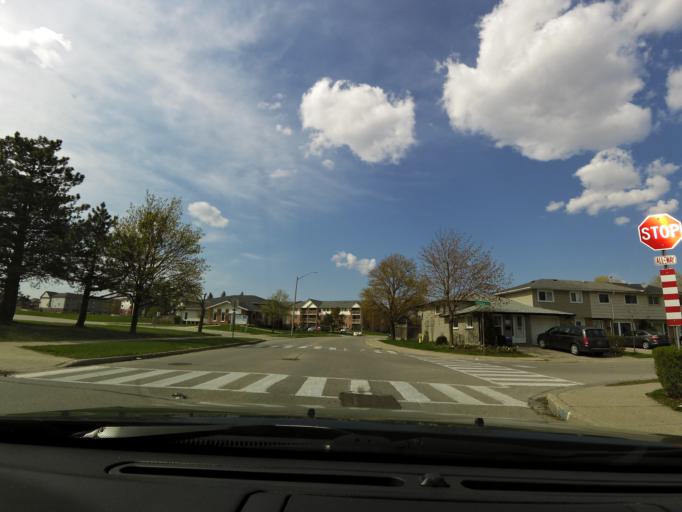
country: CA
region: Ontario
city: Cambridge
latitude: 43.3968
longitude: -80.3777
